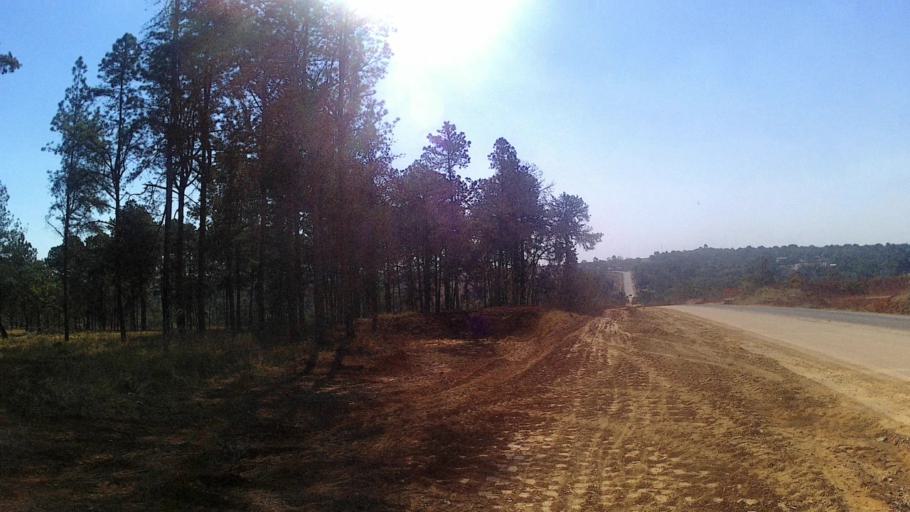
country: BR
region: Federal District
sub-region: Brasilia
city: Brasilia
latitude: -15.6795
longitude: -48.2292
